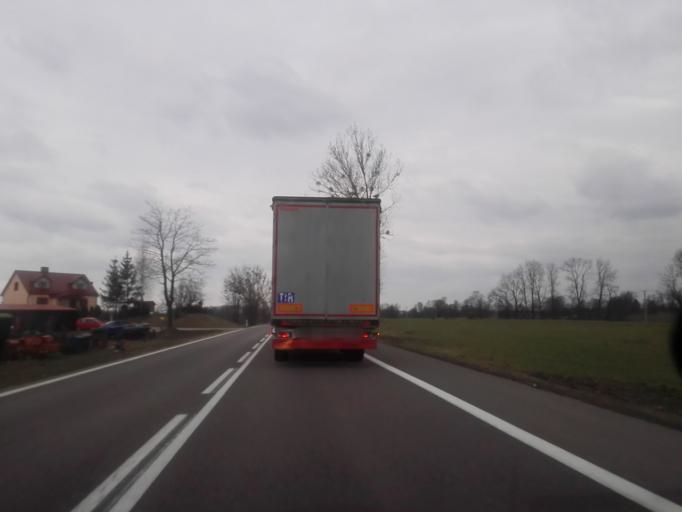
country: PL
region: Podlasie
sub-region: Powiat augustowski
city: Augustow
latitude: 53.7929
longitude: 22.8689
